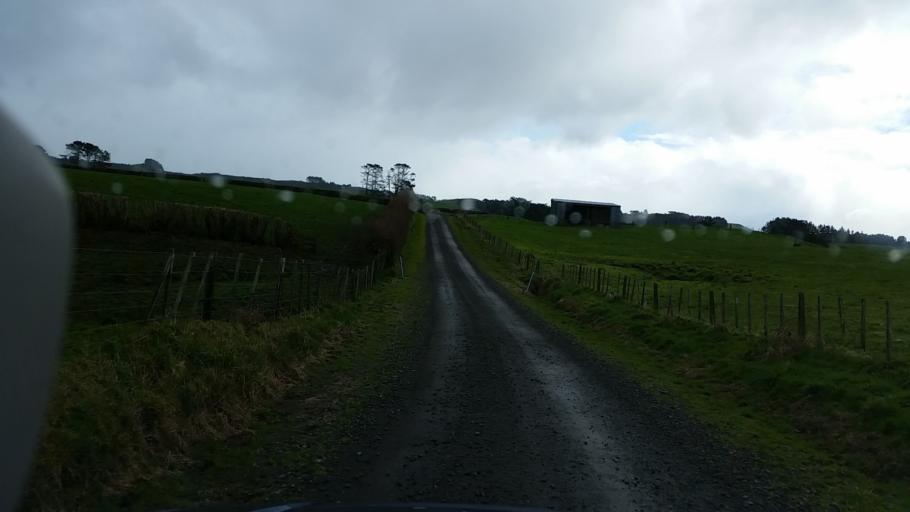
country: NZ
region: Taranaki
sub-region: South Taranaki District
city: Eltham
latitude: -39.2823
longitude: 174.3372
